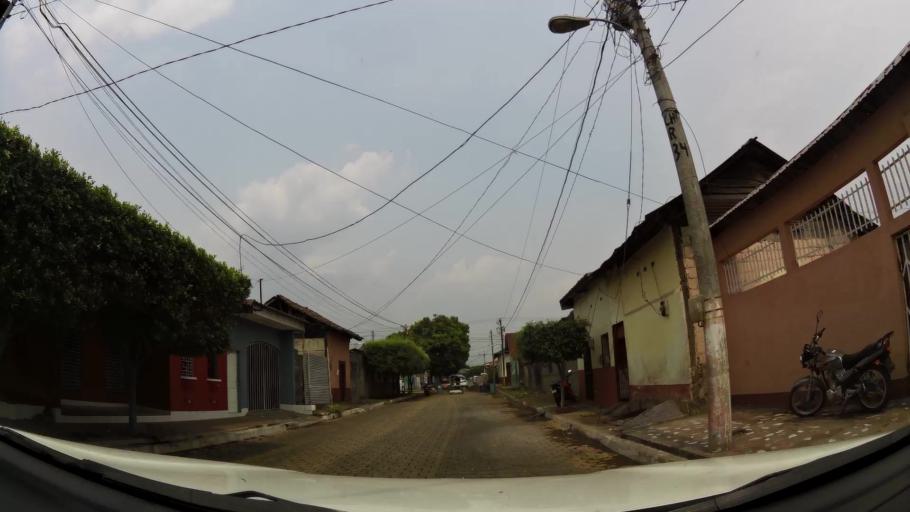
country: NI
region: Chinandega
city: Chinandega
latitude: 12.6250
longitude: -87.1359
